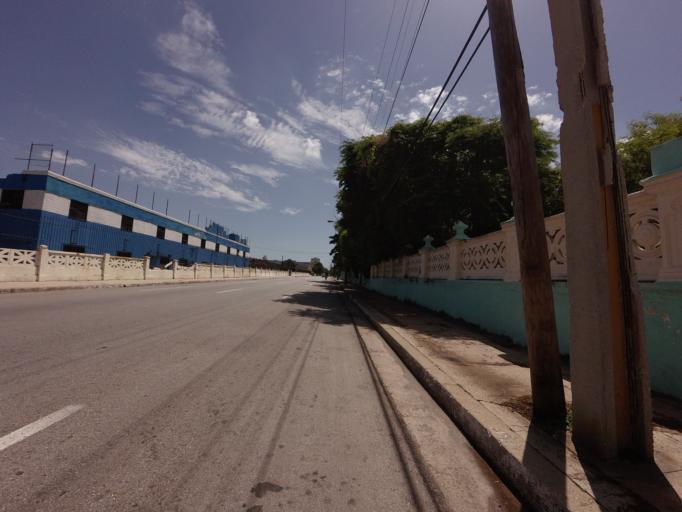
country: CU
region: La Habana
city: Havana
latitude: 23.1327
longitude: -82.4072
